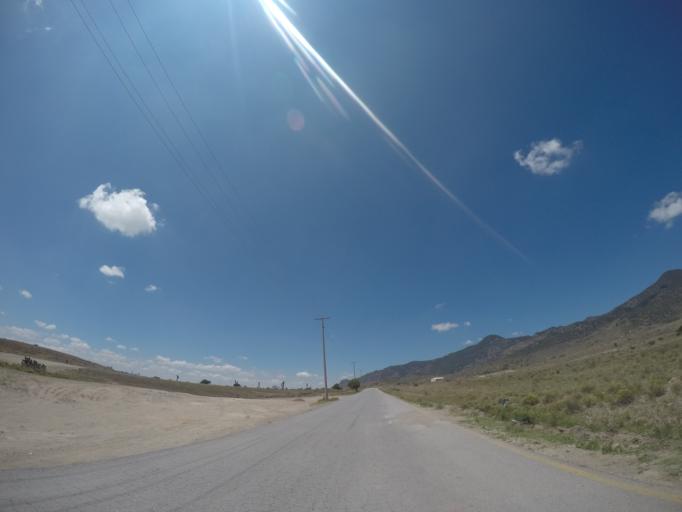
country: MX
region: San Luis Potosi
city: La Pila
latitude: 22.0164
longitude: -100.9091
